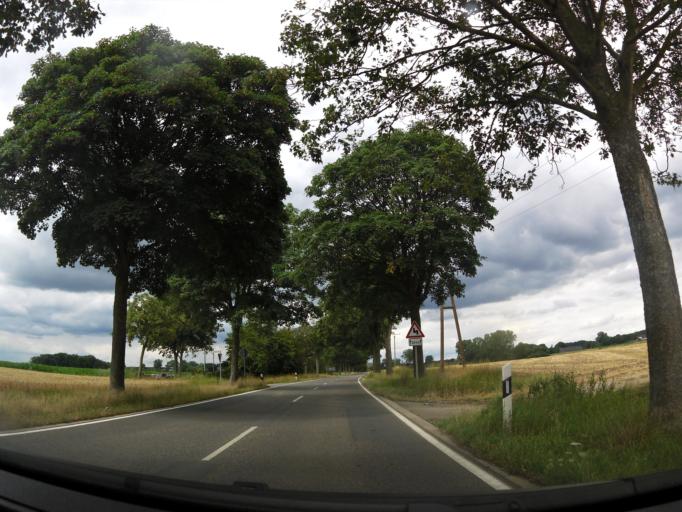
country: DE
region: North Rhine-Westphalia
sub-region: Regierungsbezirk Dusseldorf
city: Sonsbeck
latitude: 51.5762
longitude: 6.3554
